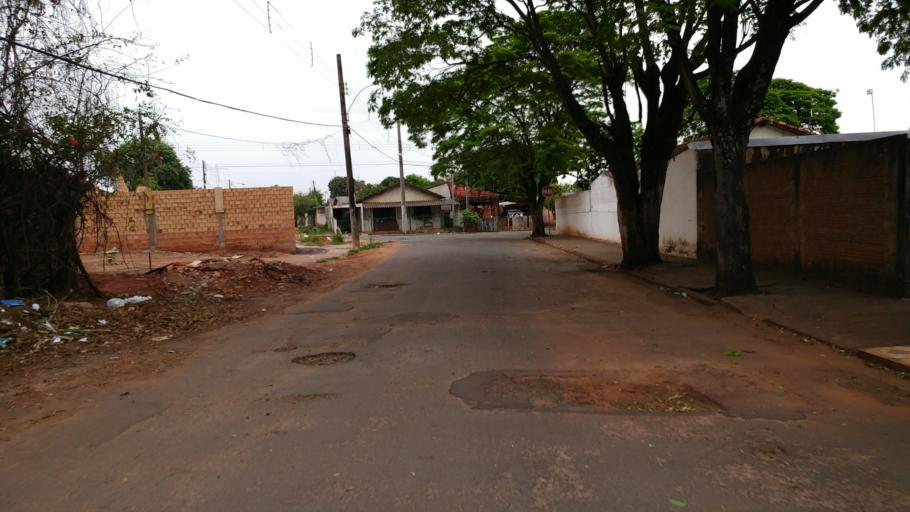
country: BR
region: Sao Paulo
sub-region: Paraguacu Paulista
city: Paraguacu Paulista
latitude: -22.4119
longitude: -50.5697
